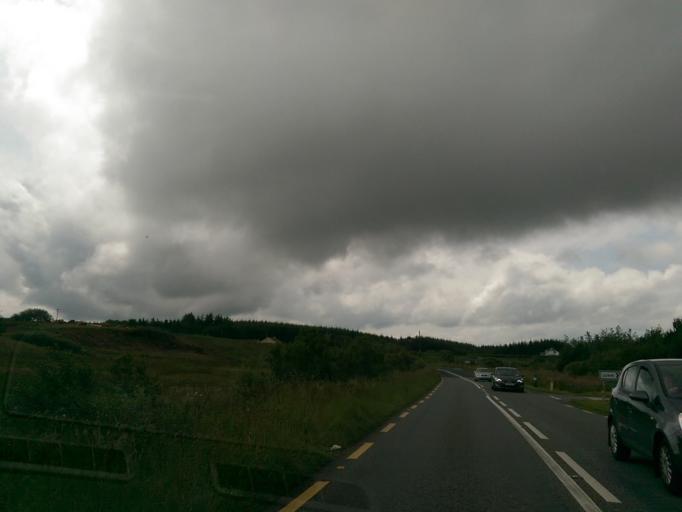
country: IE
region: Munster
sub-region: An Clar
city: Ennis
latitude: 52.7348
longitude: -9.1853
